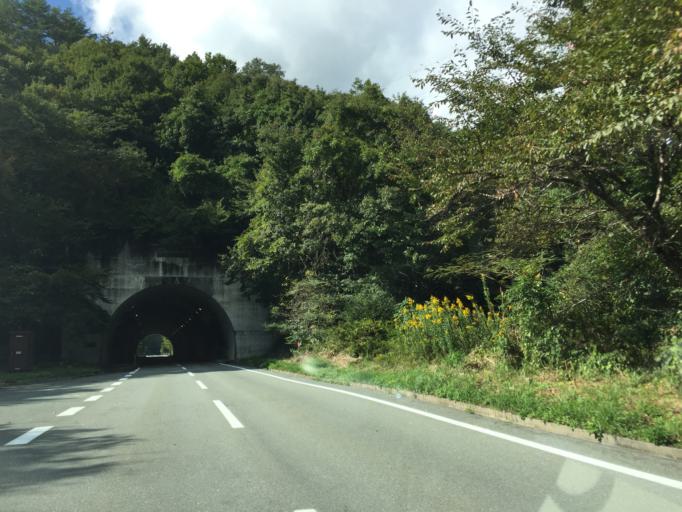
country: JP
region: Fukushima
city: Namie
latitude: 37.5244
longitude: 140.8863
